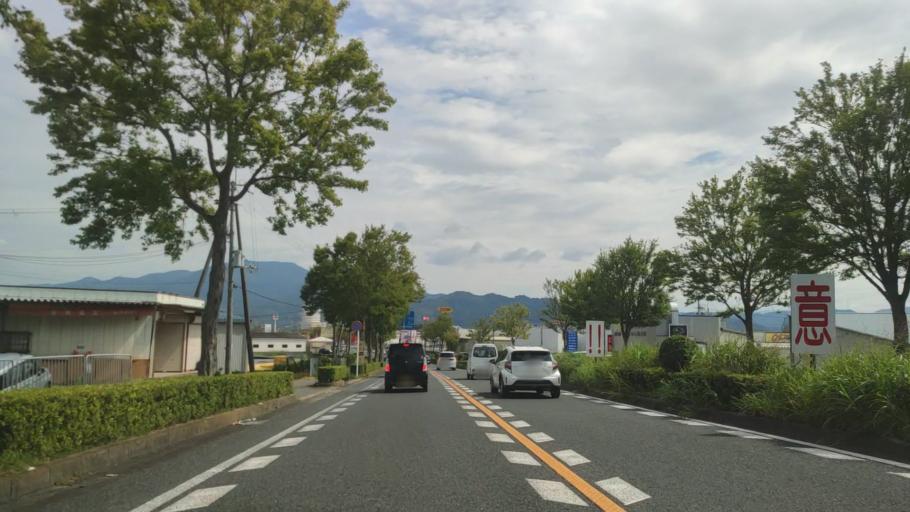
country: JP
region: Wakayama
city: Iwade
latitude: 34.2611
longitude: 135.3386
